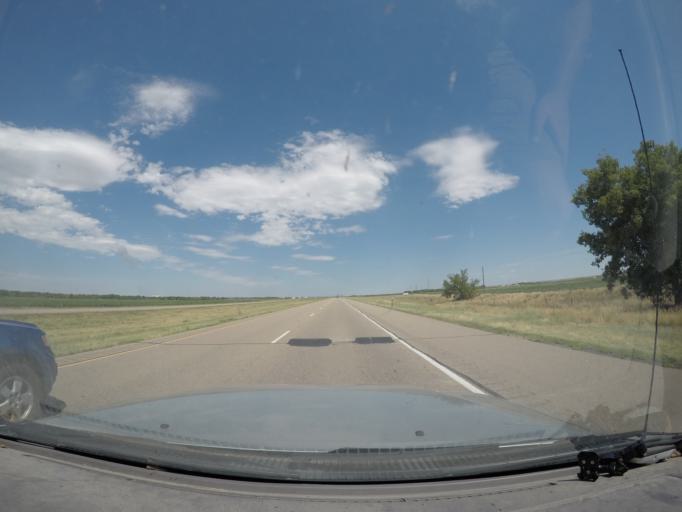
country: US
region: Colorado
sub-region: Sedgwick County
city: Julesburg
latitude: 41.0408
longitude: -102.1044
